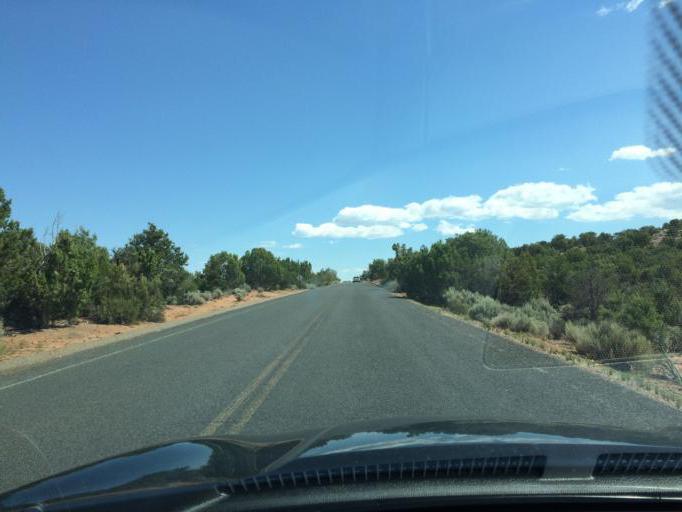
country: US
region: Arizona
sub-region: Apache County
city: Chinle
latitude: 36.0962
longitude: -109.3755
